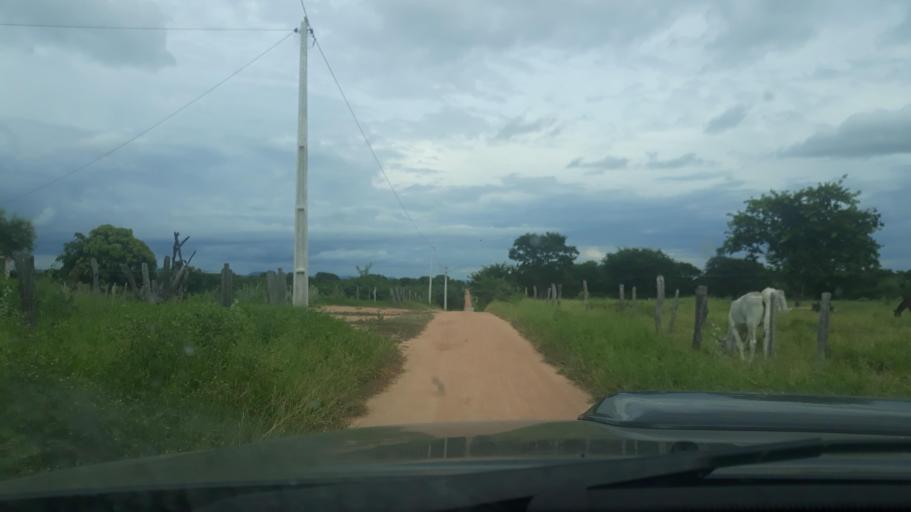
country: BR
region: Bahia
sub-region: Riacho De Santana
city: Riacho de Santana
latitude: -13.8607
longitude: -43.0322
